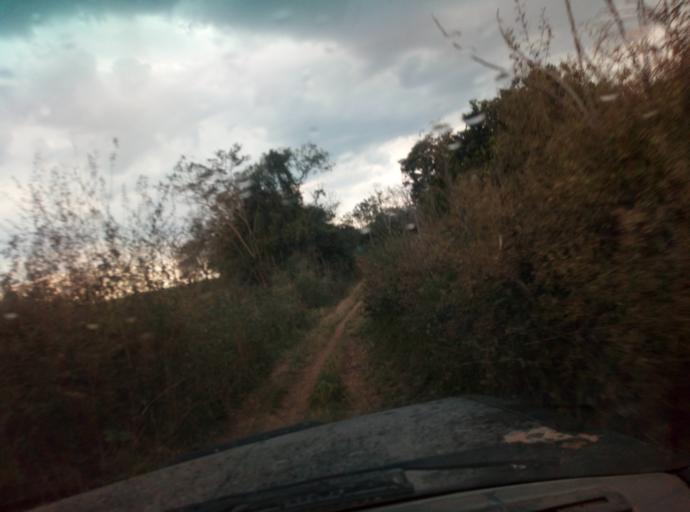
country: PY
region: Caaguazu
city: Doctor Cecilio Baez
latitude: -25.1472
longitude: -56.2221
